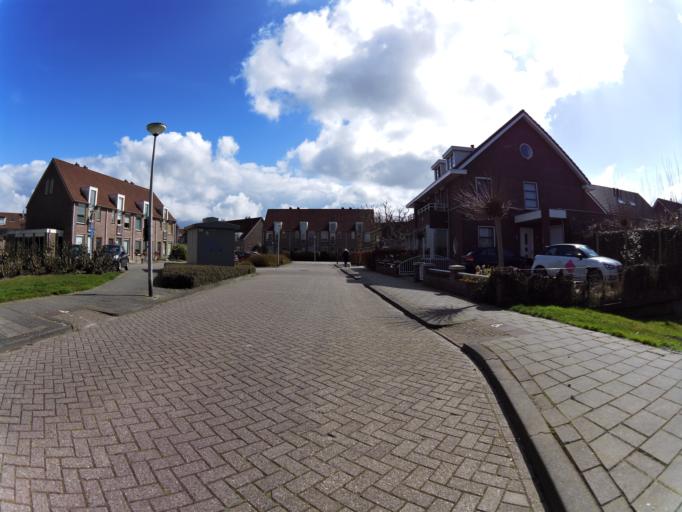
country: NL
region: South Holland
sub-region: Gemeente Hellevoetsluis
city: Nieuw-Helvoet
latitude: 51.8679
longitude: 4.0699
